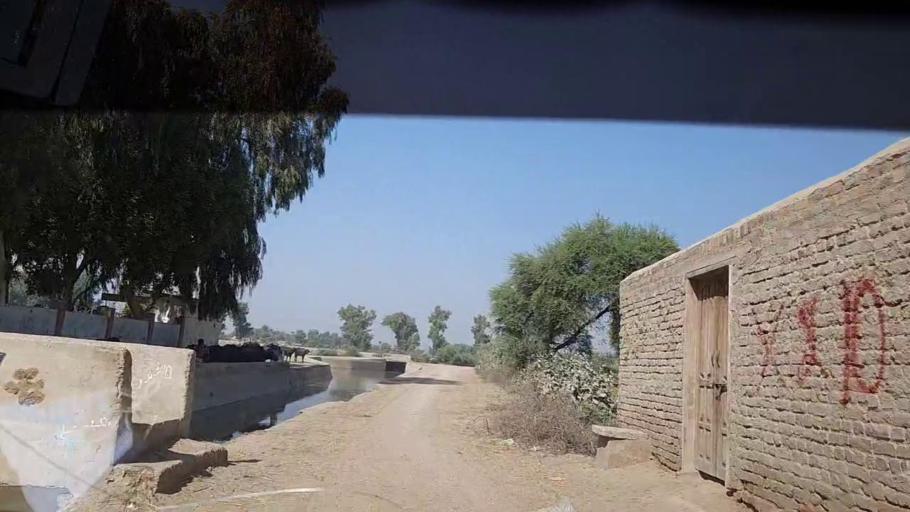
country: PK
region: Sindh
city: Naudero
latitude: 27.6624
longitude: 68.3743
